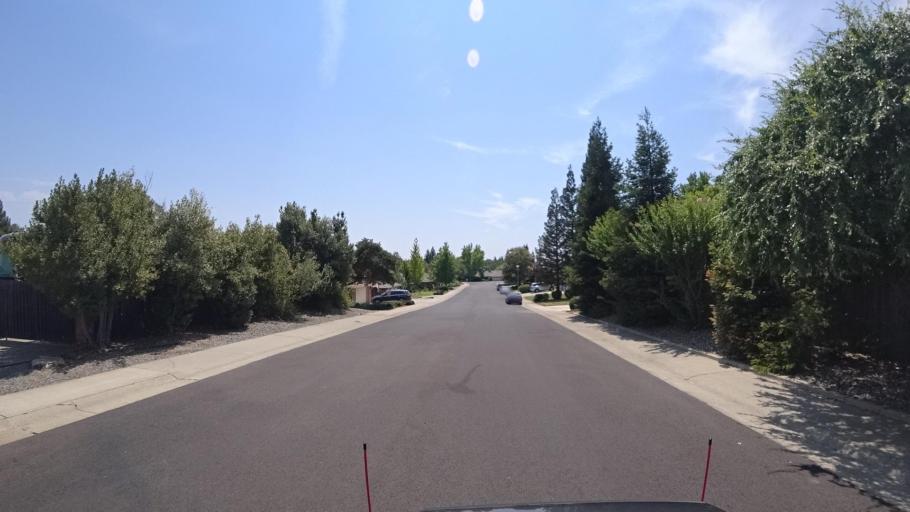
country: US
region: California
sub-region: Placer County
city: Rocklin
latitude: 38.8025
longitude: -121.2322
